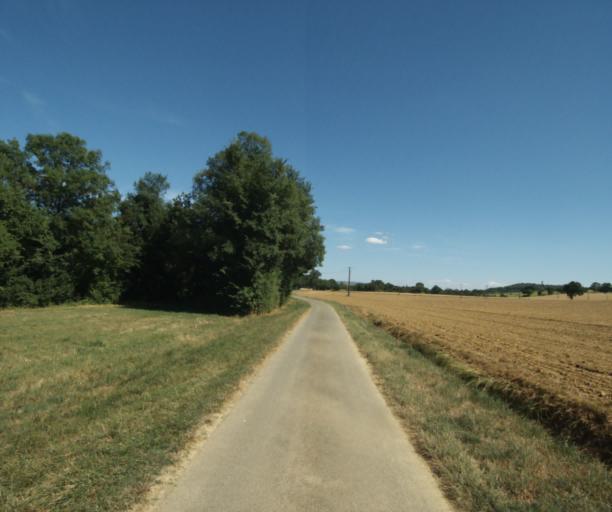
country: FR
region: Midi-Pyrenees
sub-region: Departement de la Haute-Garonne
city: Auriac-sur-Vendinelle
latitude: 43.5113
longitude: 1.8865
